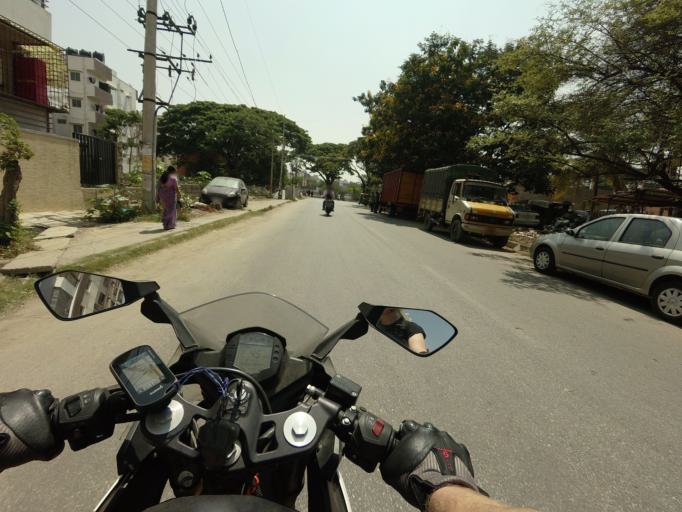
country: IN
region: Karnataka
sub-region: Bangalore Urban
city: Bangalore
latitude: 13.0118
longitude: 77.6611
